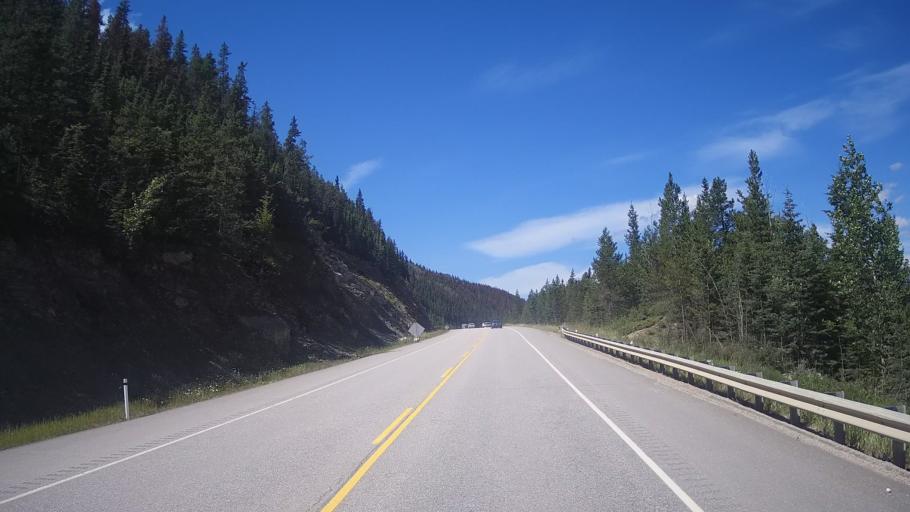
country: CA
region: Alberta
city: Jasper Park Lodge
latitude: 52.8768
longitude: -118.3299
